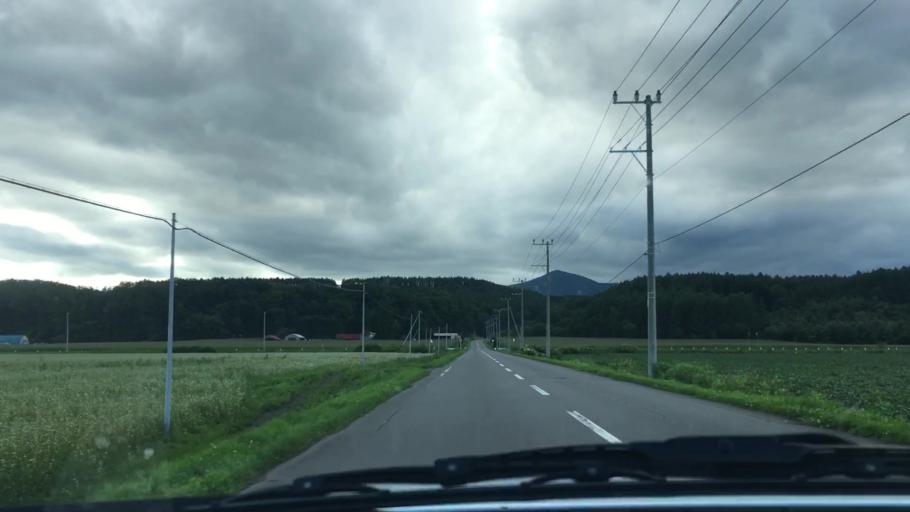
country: JP
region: Hokkaido
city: Otofuke
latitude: 43.1402
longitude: 142.8916
